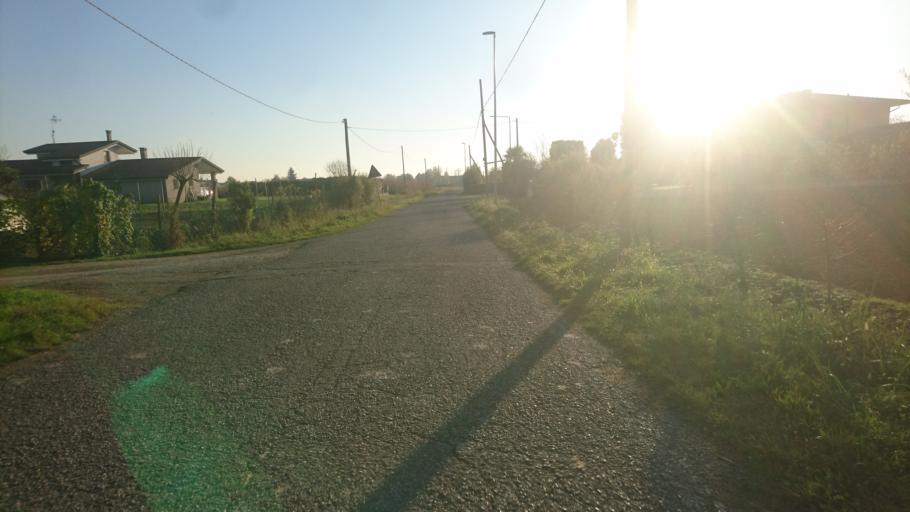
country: IT
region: Veneto
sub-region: Provincia di Padova
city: Bosco
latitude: 45.4439
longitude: 11.8051
